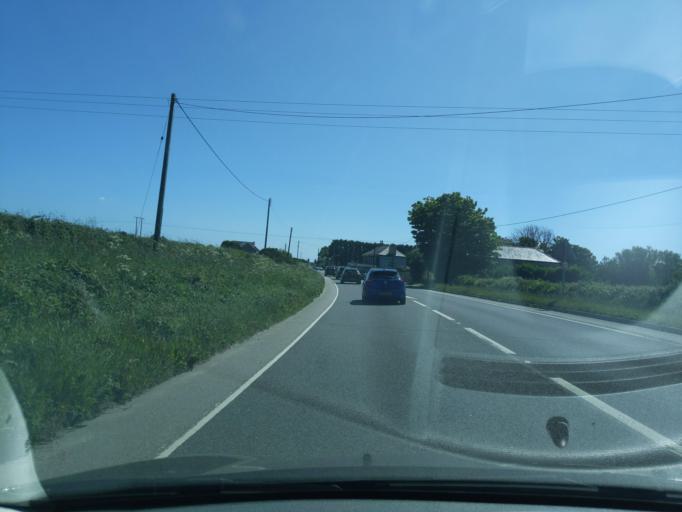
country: GB
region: England
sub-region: Cornwall
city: Wendron
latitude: 50.1604
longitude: -5.1850
